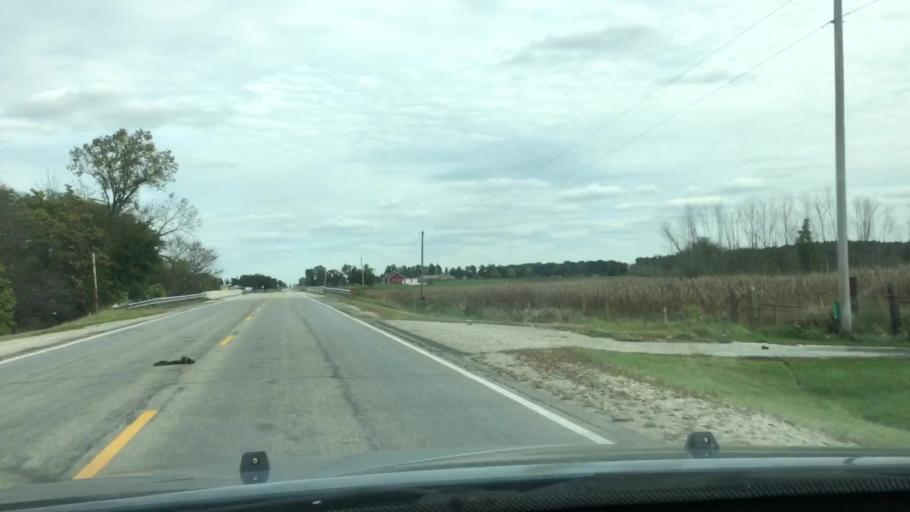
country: US
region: Indiana
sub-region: Adams County
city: Geneva
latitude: 40.5417
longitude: -84.9199
